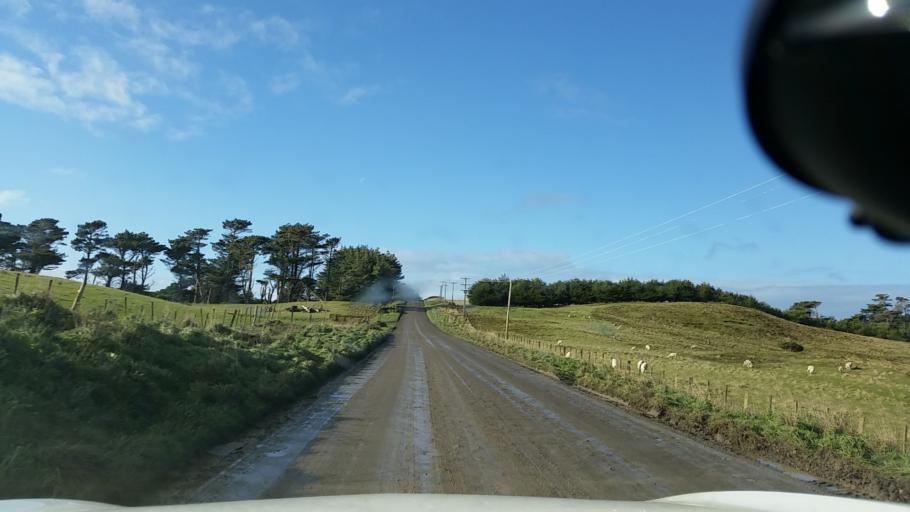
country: NZ
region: Chatham Islands
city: Waitangi
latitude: -43.9713
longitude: -176.5172
